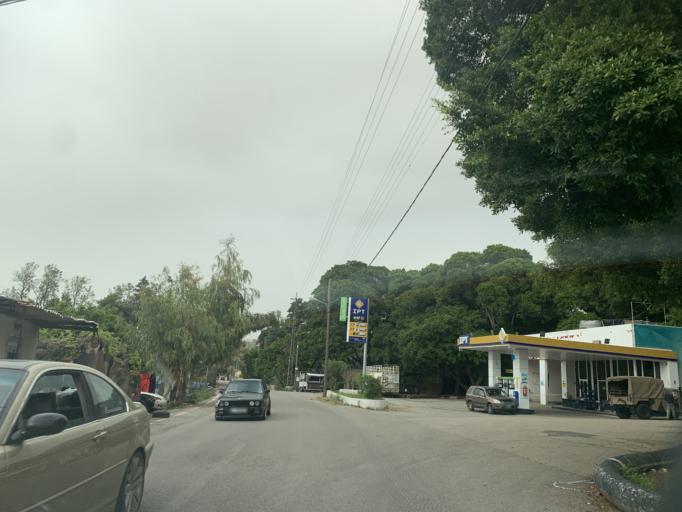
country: LB
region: Mont-Liban
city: Jbail
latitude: 34.1513
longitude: 35.6311
